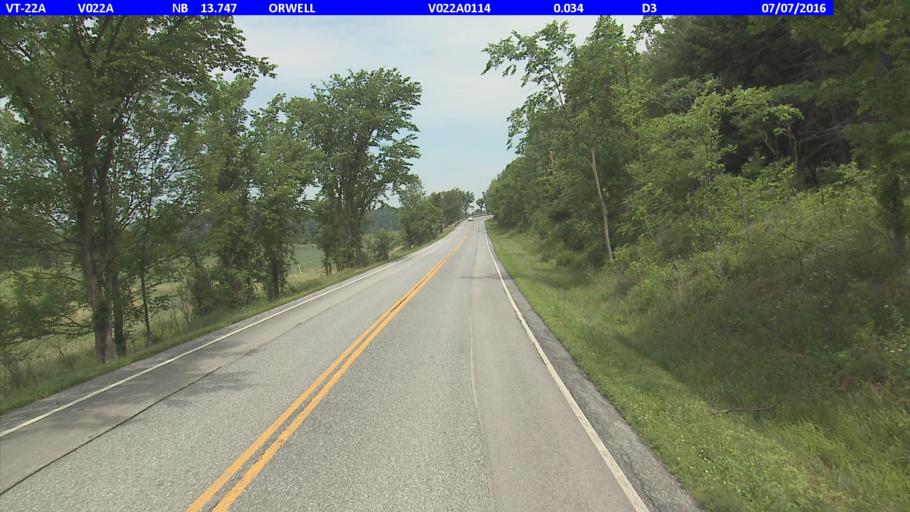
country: US
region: New York
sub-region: Essex County
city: Ticonderoga
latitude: 43.7579
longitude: -73.3115
